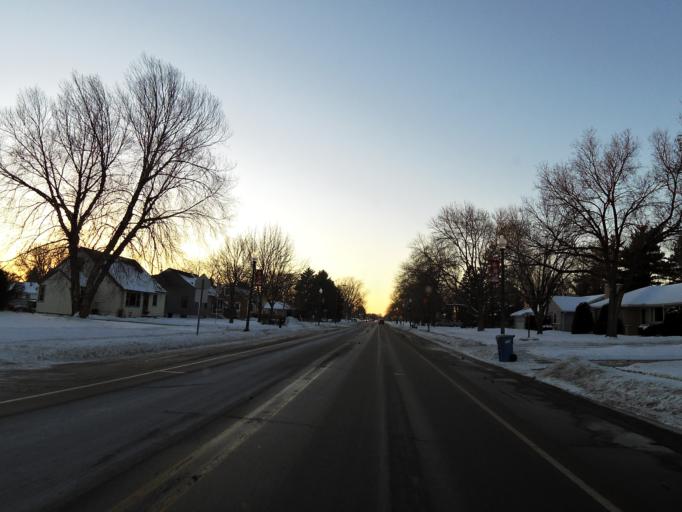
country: US
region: Minnesota
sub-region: Dakota County
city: Rosemount
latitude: 44.7392
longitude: -93.1325
